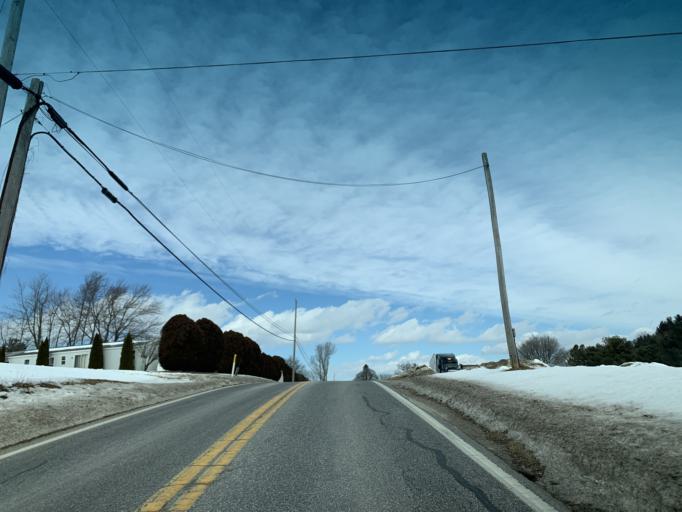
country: US
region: Pennsylvania
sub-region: York County
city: Shrewsbury
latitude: 39.7925
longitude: -76.6352
